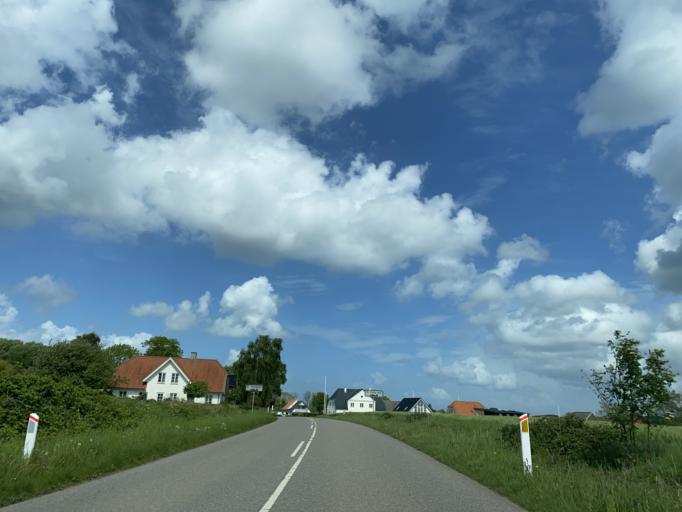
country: DK
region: South Denmark
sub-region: Sonderborg Kommune
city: Dybbol
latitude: 54.9732
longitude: 9.7137
